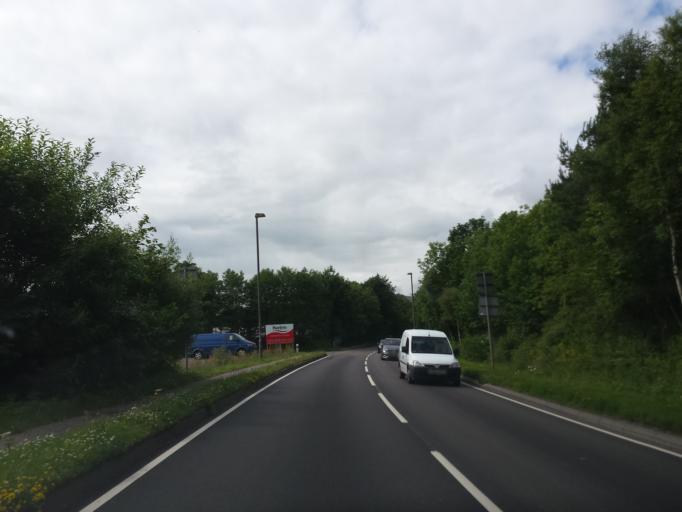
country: GB
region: Scotland
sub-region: Highland
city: Fort William
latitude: 56.8434
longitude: -5.1478
